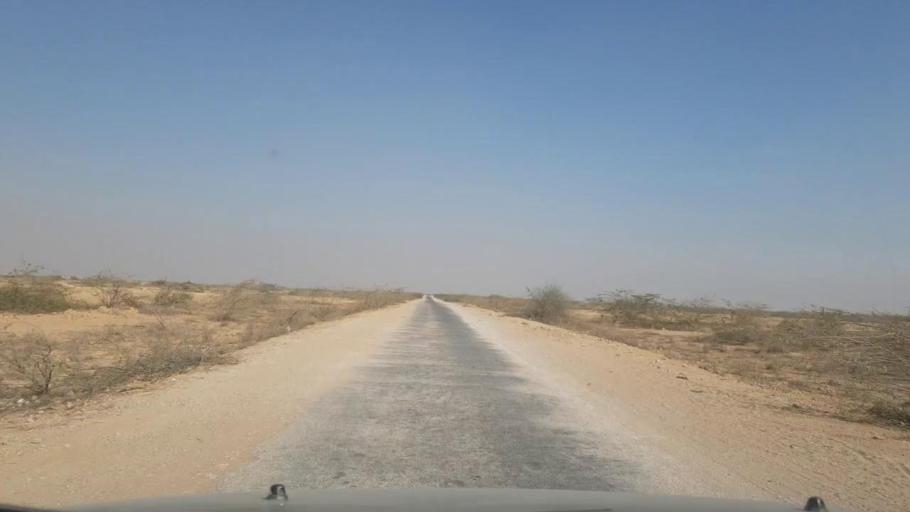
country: PK
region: Sindh
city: Thatta
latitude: 24.8940
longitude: 67.9161
